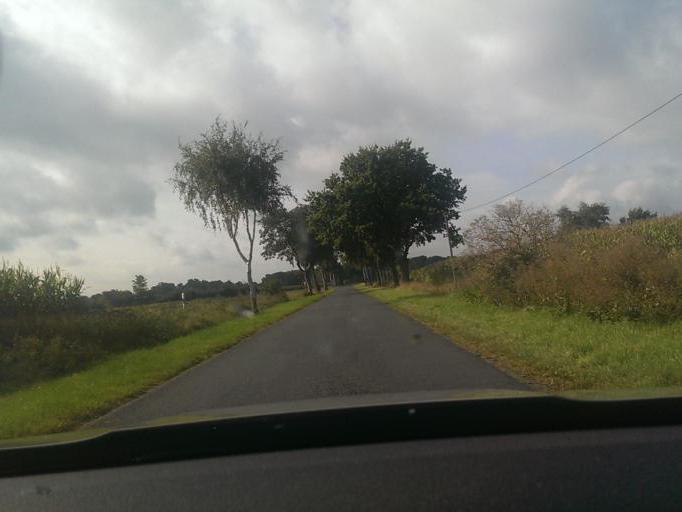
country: DE
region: Lower Saxony
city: Elze
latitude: 52.5737
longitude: 9.7676
